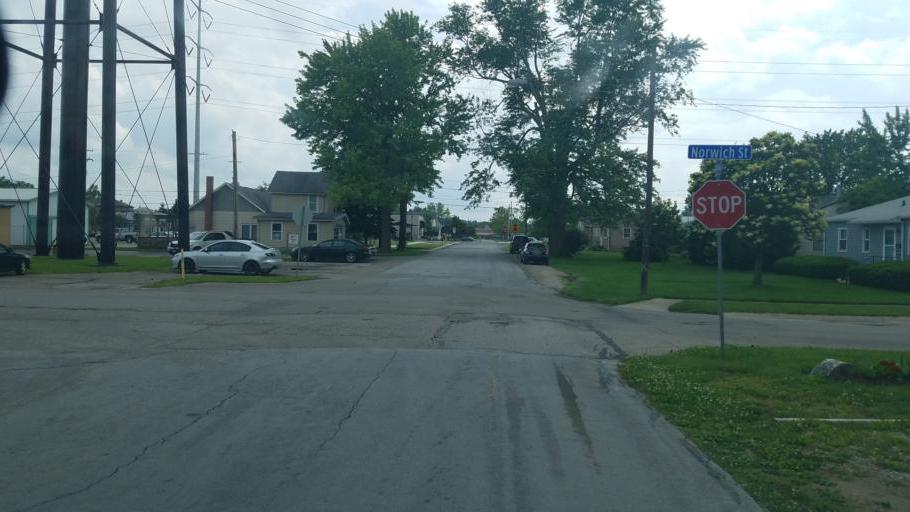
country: US
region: Ohio
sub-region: Franklin County
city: Hilliard
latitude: 40.0355
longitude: -83.1596
